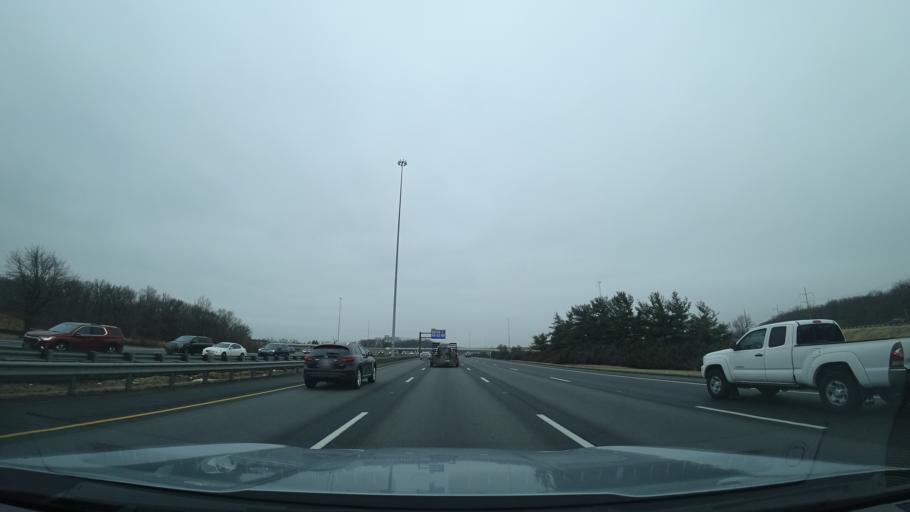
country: US
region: Delaware
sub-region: New Castle County
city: Bear
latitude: 39.6756
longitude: -75.6713
